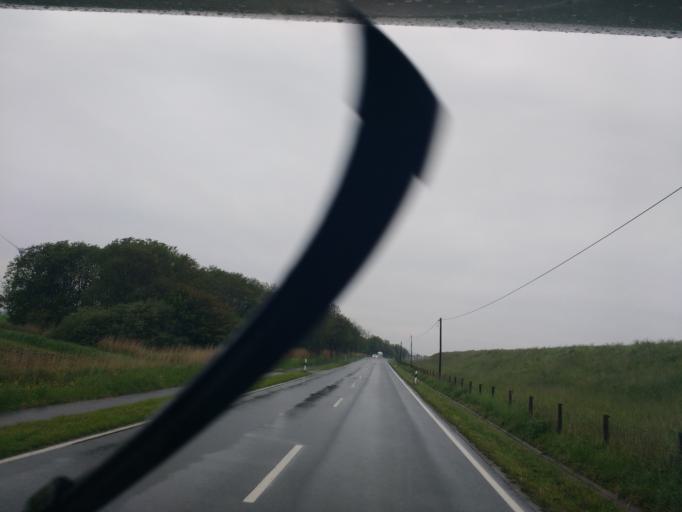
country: DE
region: Lower Saxony
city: Neuharlingersiel
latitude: 53.6944
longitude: 7.7447
